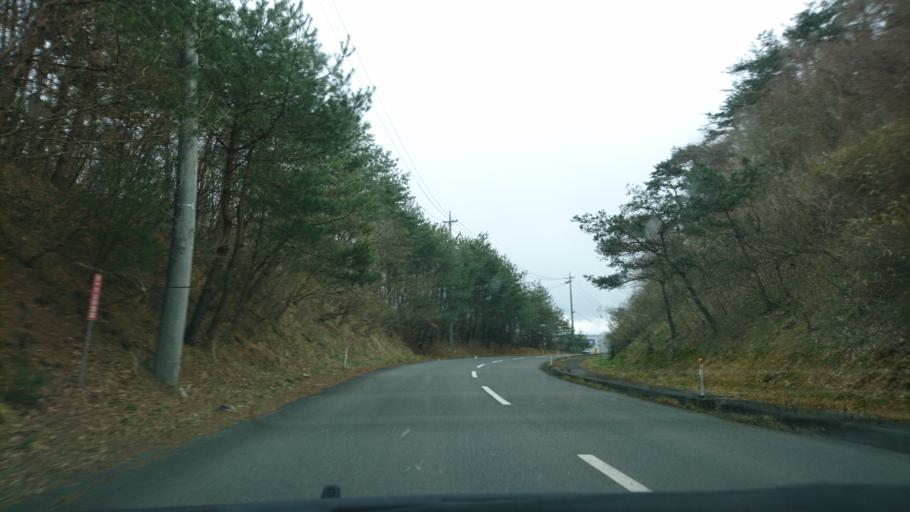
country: JP
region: Iwate
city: Ichinoseki
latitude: 38.8314
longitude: 141.1719
